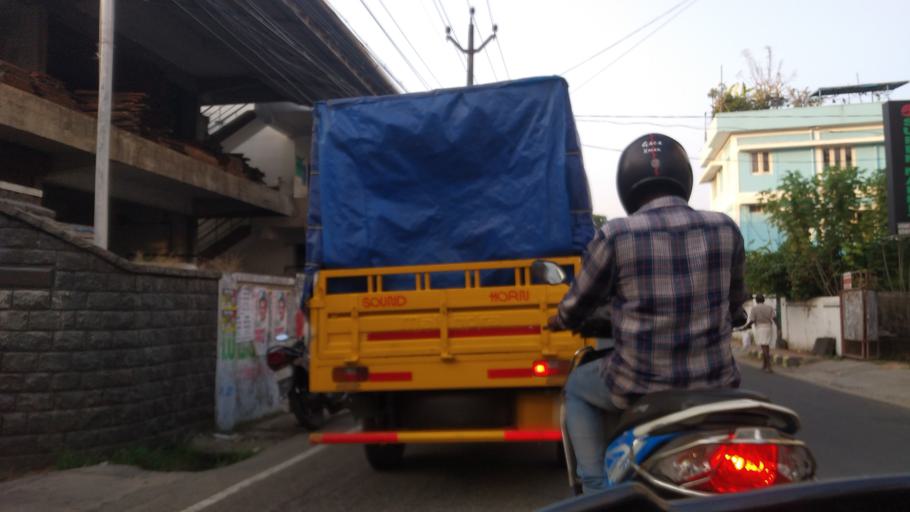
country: IN
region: Kerala
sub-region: Ernakulam
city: Elur
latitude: 10.0233
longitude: 76.2739
